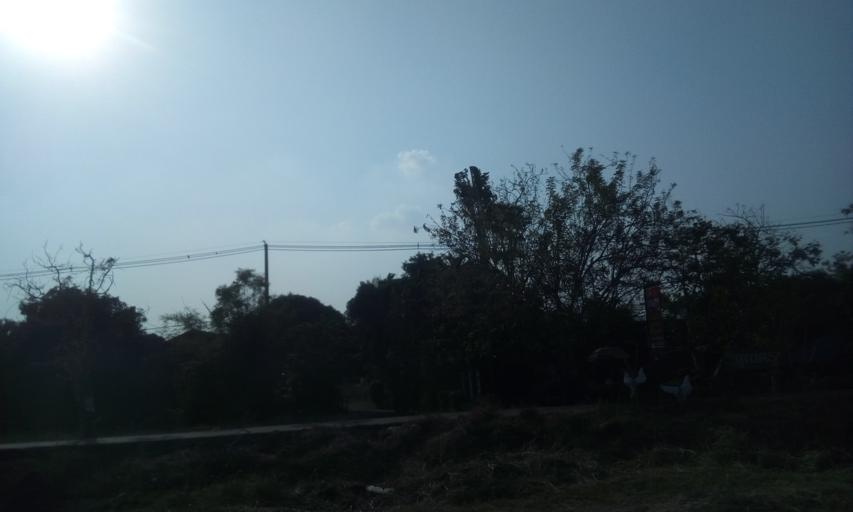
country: TH
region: Sing Buri
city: Sing Buri
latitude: 14.8686
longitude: 100.4051
